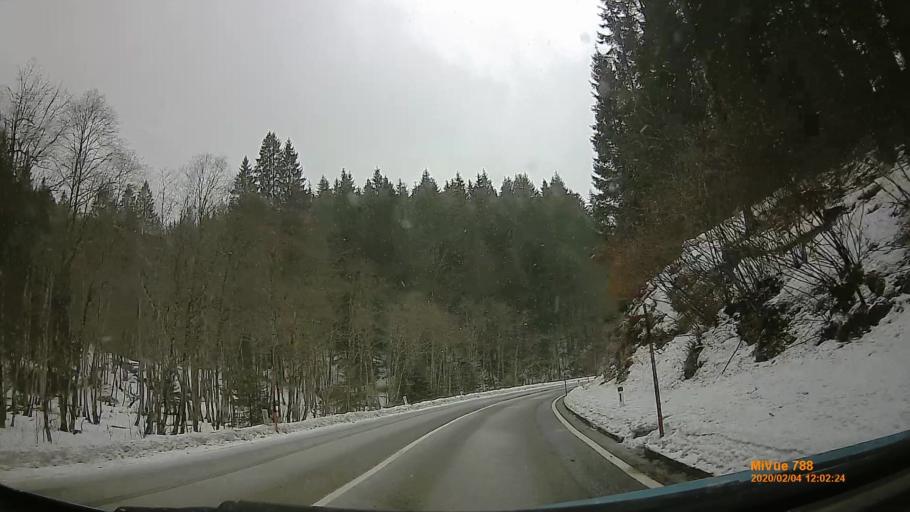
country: AT
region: Styria
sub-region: Politischer Bezirk Bruck-Muerzzuschlag
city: Muerzsteg
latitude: 47.7701
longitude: 15.4619
